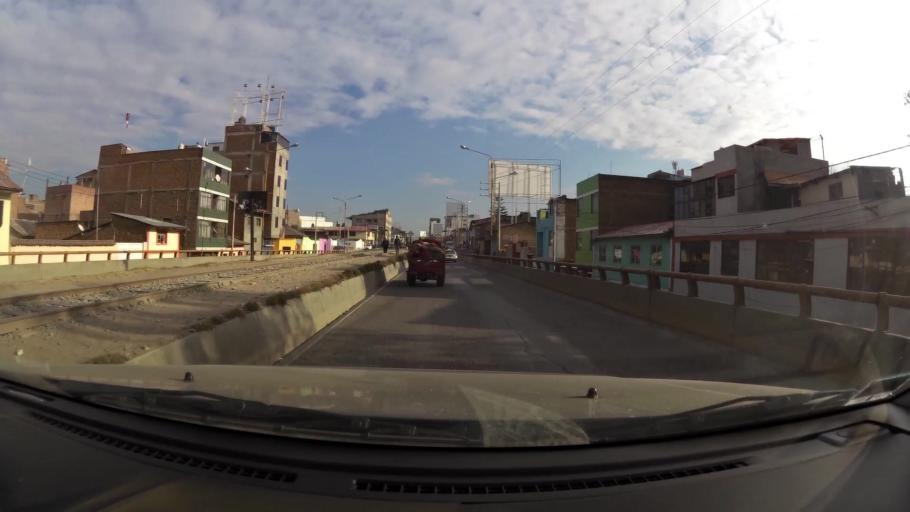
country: PE
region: Junin
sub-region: Provincia de Huancayo
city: Huancayo
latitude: -12.0660
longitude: -75.2064
